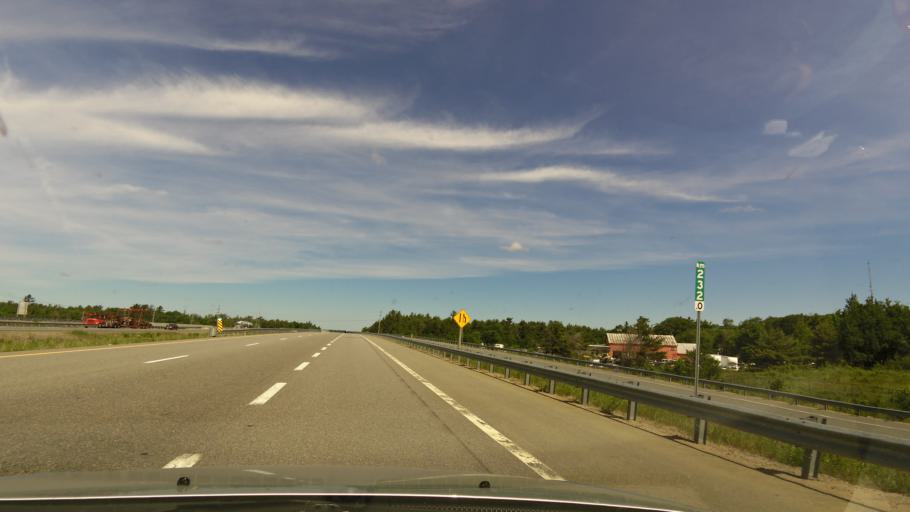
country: CA
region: Ontario
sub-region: Parry Sound District
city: Parry Sound
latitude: 45.3835
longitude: -80.0428
